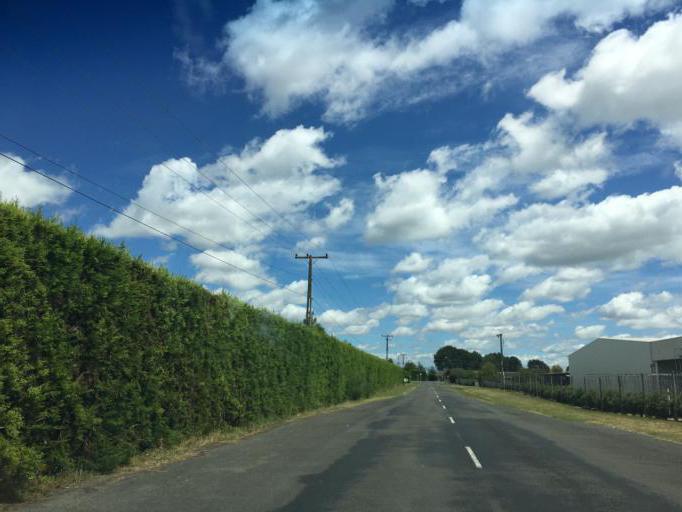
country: NZ
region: Hawke's Bay
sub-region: Hastings District
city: Hastings
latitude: -39.6554
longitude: 176.8898
